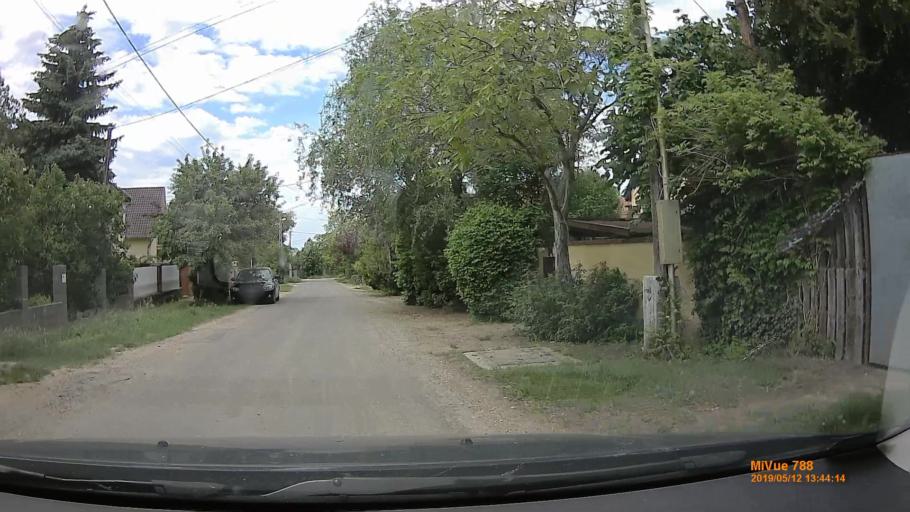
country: HU
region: Budapest
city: Budapest XVII. keruelet
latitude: 47.4835
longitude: 19.2965
